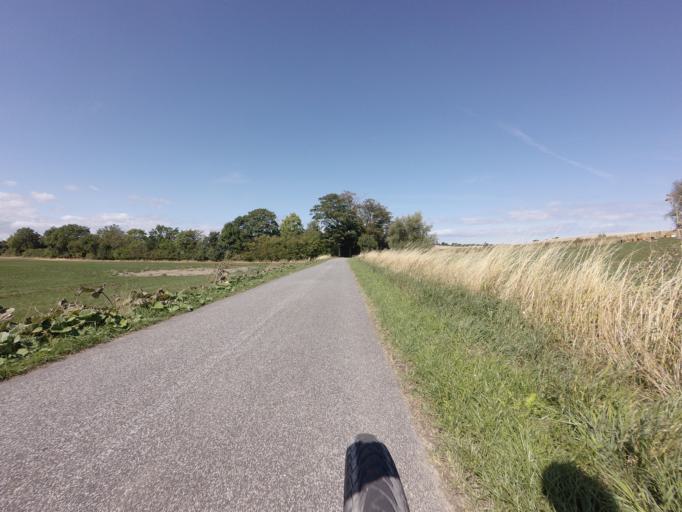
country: DK
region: Zealand
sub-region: Vordingborg Kommune
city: Stege
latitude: 55.0011
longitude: 12.4763
